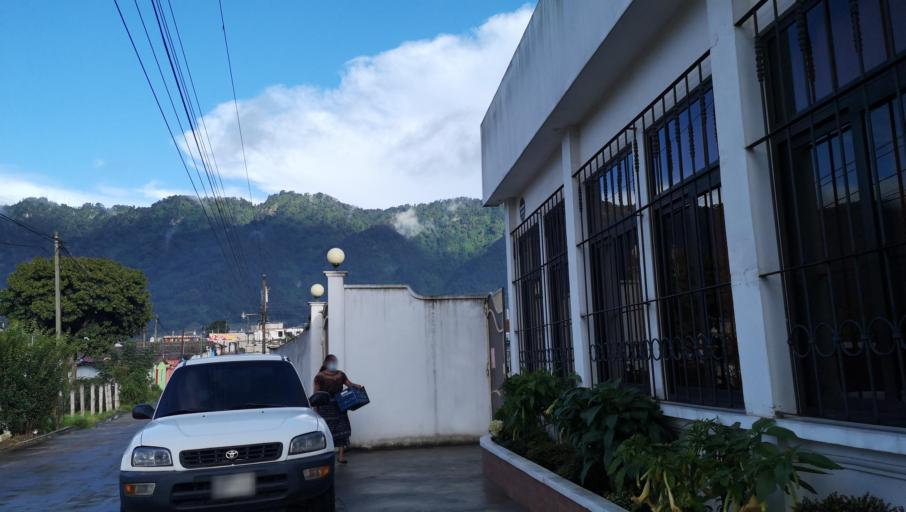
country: GT
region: Quetzaltenango
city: Cantel
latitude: 14.8187
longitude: -91.4431
